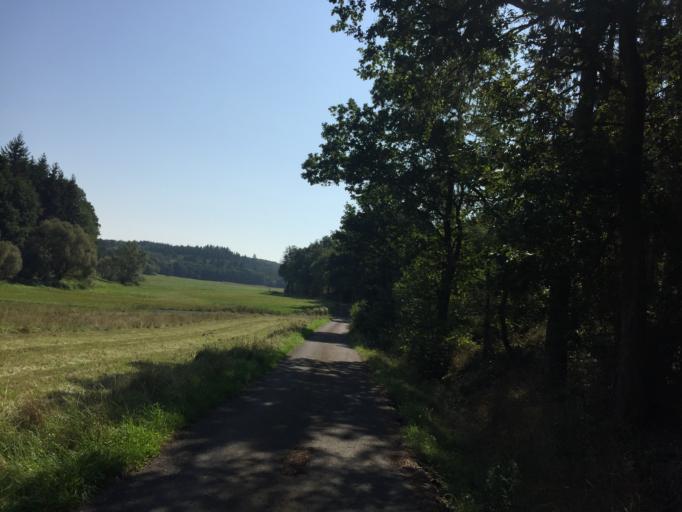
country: DE
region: Hesse
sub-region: Regierungsbezirk Darmstadt
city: Butzbach
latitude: 50.4342
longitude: 8.5904
